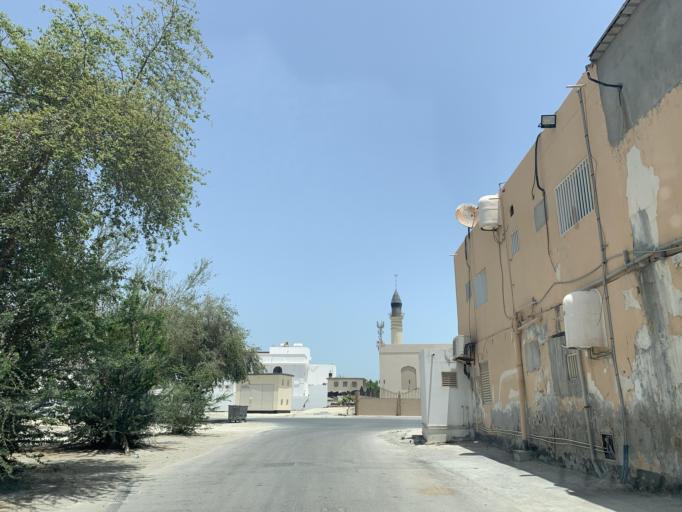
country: BH
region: Northern
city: Sitrah
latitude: 26.1708
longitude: 50.6102
